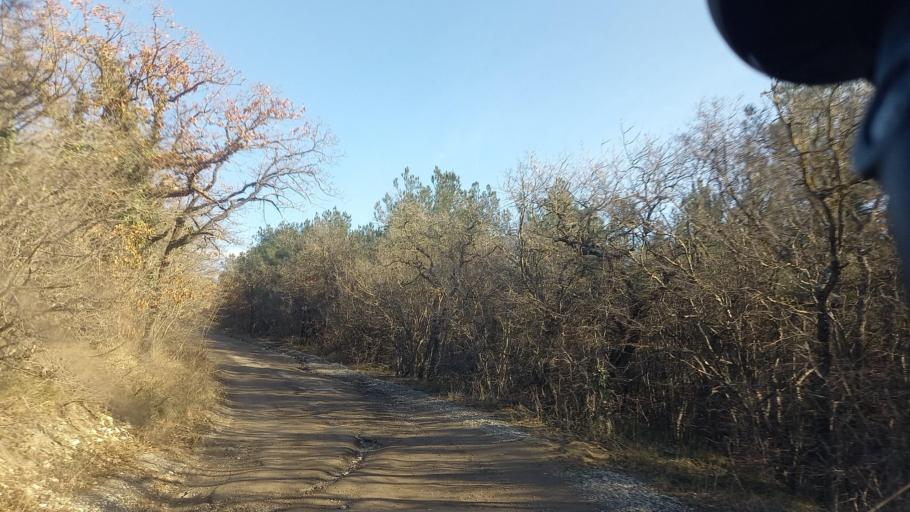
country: RU
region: Krasnodarskiy
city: Kabardinka
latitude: 44.6296
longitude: 37.9197
